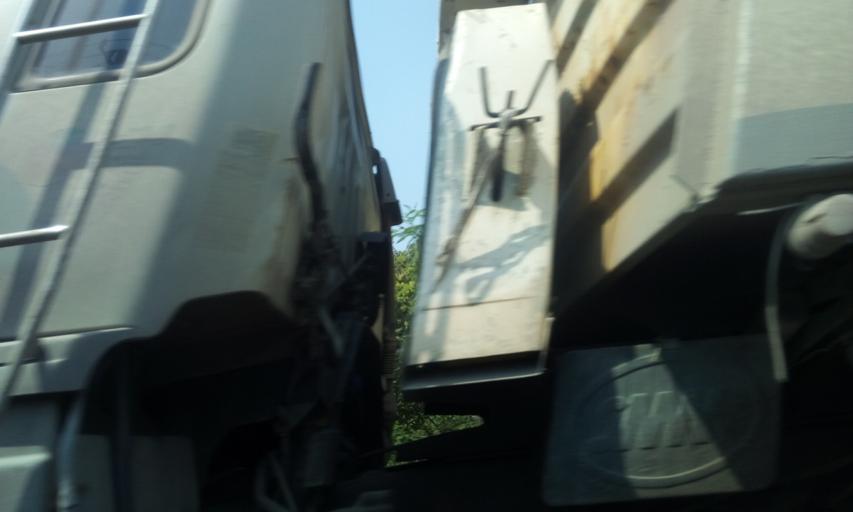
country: TH
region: Nakhon Nayok
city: Ongkharak
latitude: 14.1453
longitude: 100.9821
